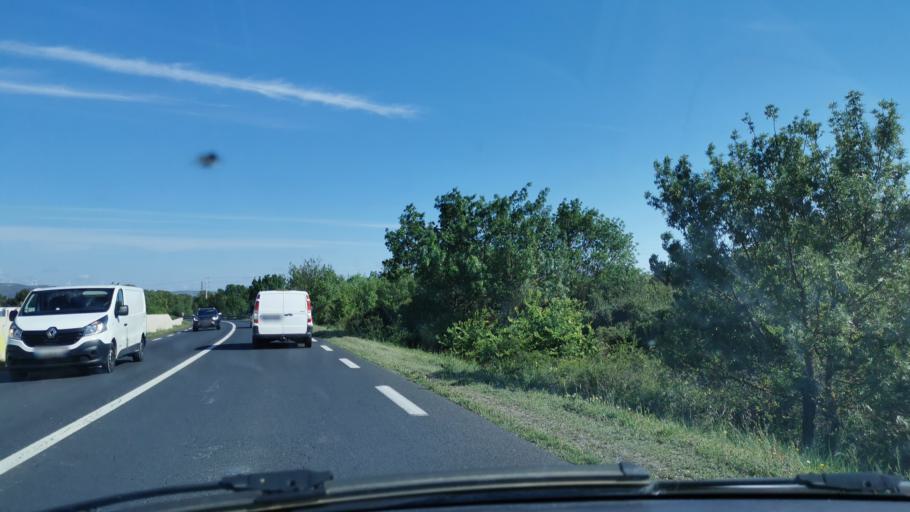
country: FR
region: Languedoc-Roussillon
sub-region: Departement de l'Herault
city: Balaruc-le-Vieux
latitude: 43.4654
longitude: 3.6925
